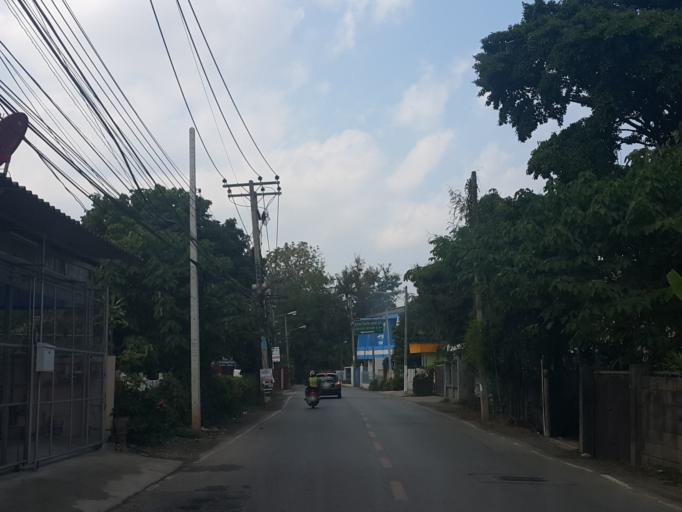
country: TH
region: Chiang Mai
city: Chiang Mai
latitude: 18.8310
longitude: 98.9935
